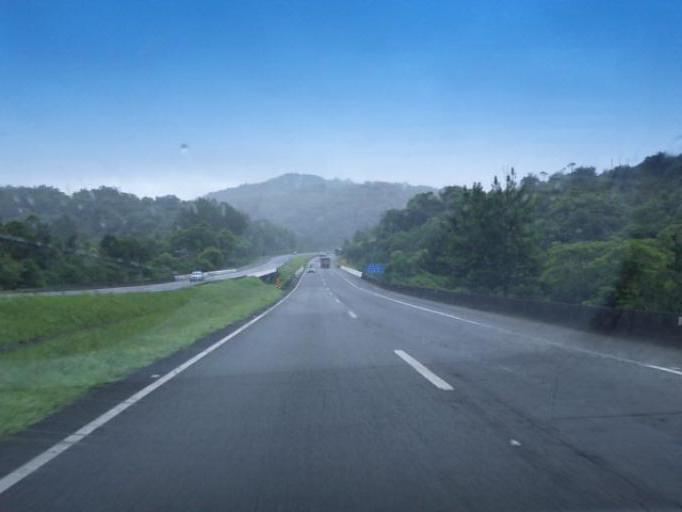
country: BR
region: Parana
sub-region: Antonina
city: Antonina
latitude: -25.0821
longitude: -48.6265
